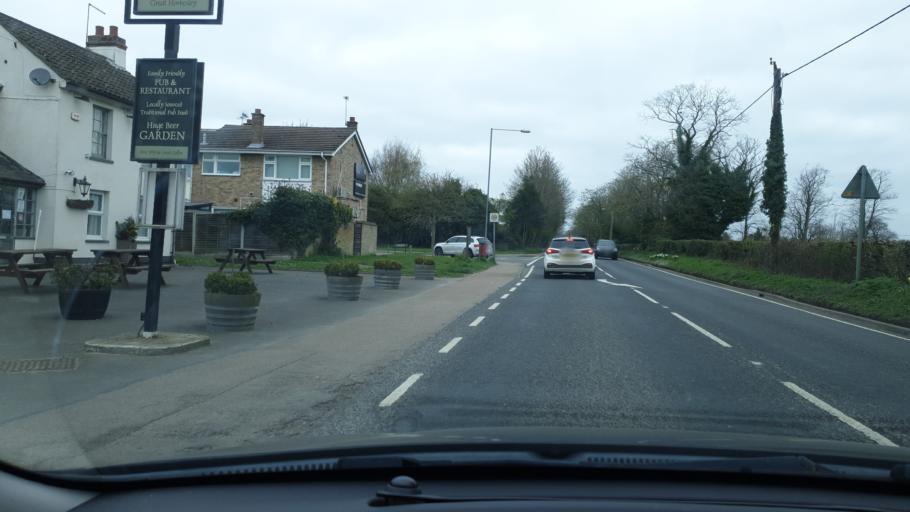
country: GB
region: England
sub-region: Essex
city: Great Horkesley
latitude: 51.9263
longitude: 0.8809
